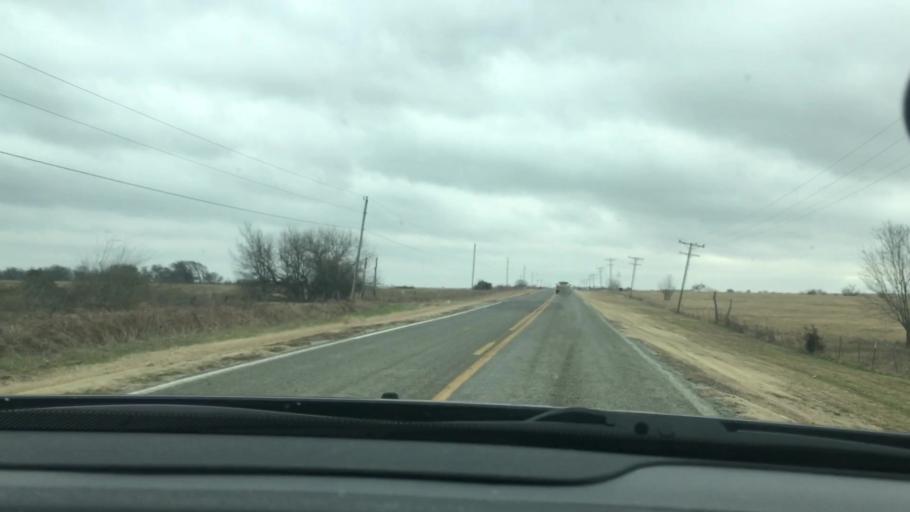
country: US
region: Oklahoma
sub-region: Johnston County
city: Tishomingo
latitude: 34.1433
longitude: -96.5375
